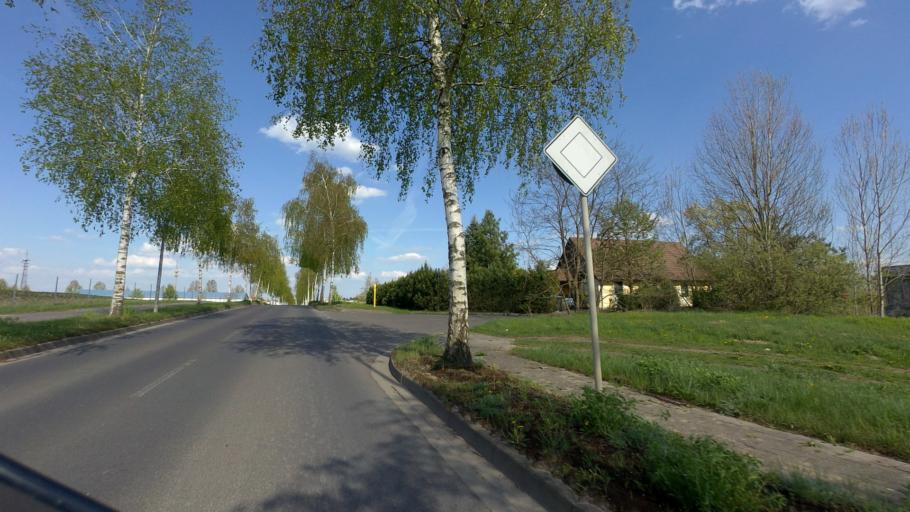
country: DE
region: Brandenburg
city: Templin
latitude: 53.1064
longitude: 13.4896
